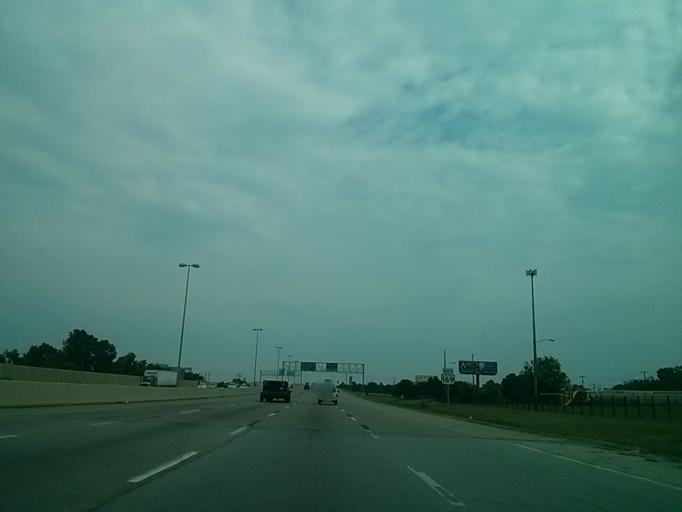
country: US
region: Oklahoma
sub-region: Tulsa County
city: Broken Arrow
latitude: 36.1431
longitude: -95.8600
